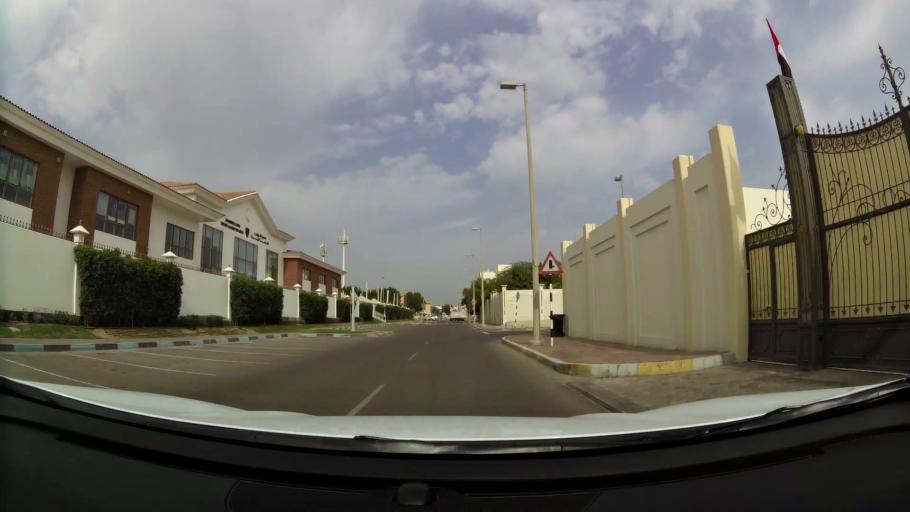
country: AE
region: Abu Dhabi
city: Abu Dhabi
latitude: 24.4537
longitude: 54.3726
